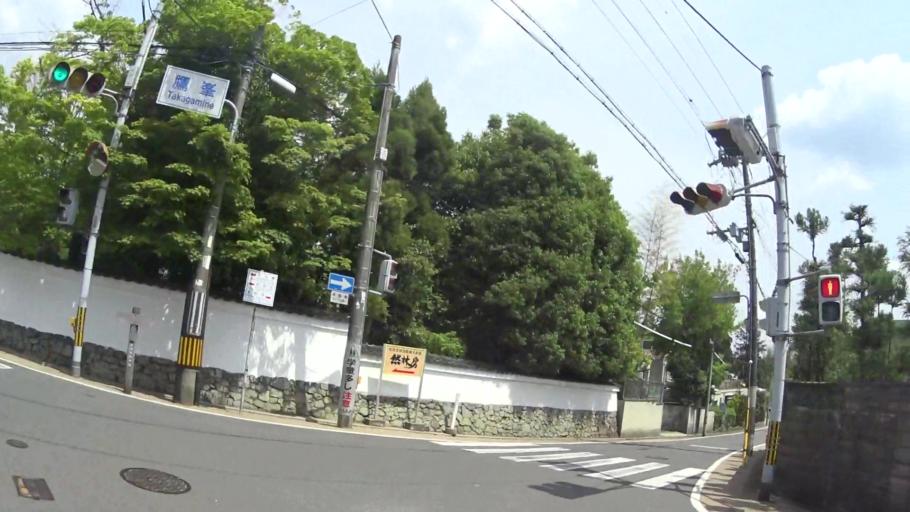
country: JP
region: Kyoto
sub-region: Kyoto-shi
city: Kamigyo-ku
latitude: 35.0541
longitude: 135.7320
